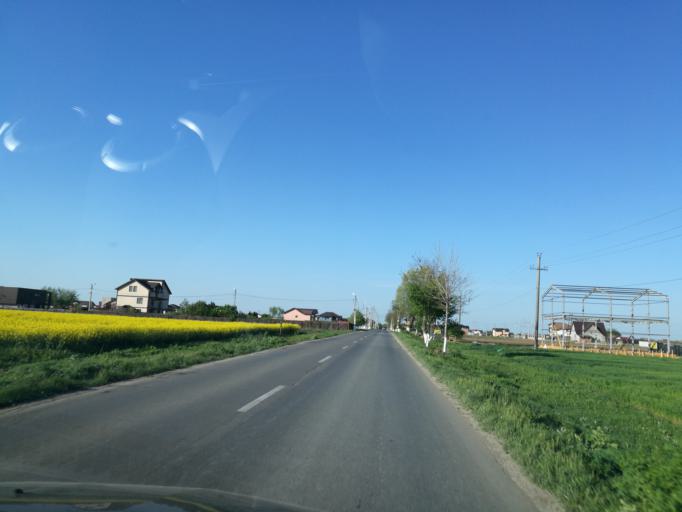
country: RO
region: Ilfov
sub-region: Comuna Berceni
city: Berceni
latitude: 44.2876
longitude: 26.1840
